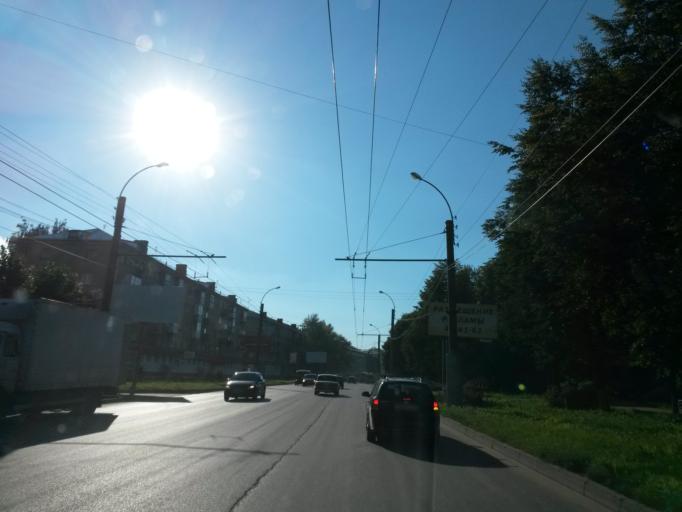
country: RU
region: Ivanovo
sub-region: Gorod Ivanovo
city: Ivanovo
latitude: 56.9829
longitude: 40.9673
